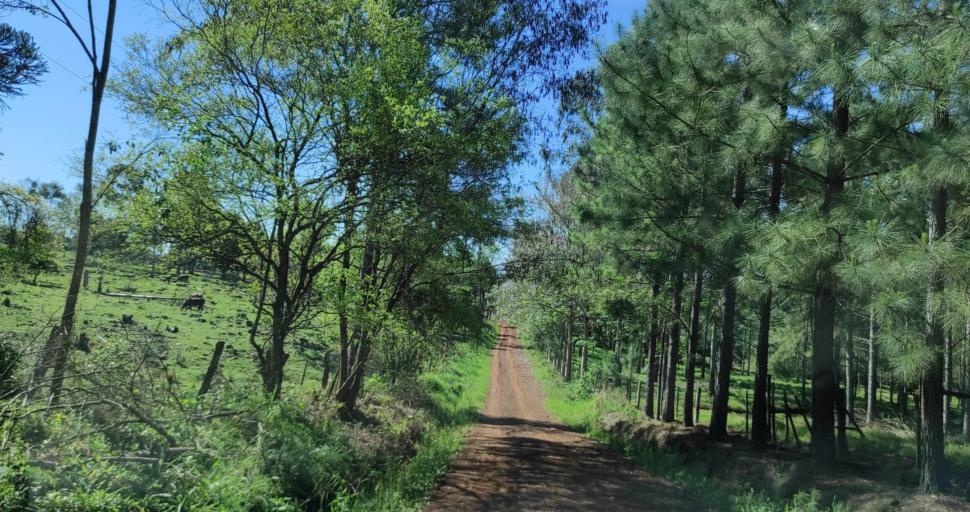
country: AR
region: Misiones
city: Capiovi
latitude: -26.9372
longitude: -55.0018
